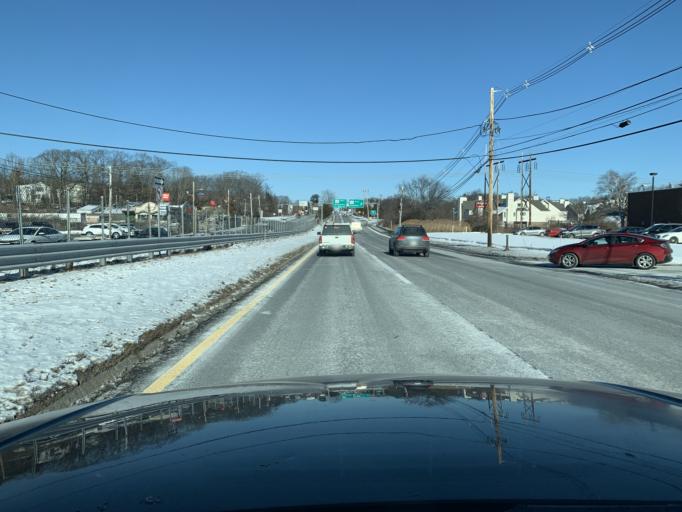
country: US
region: Massachusetts
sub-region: Essex County
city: Danvers
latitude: 42.5580
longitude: -70.9786
